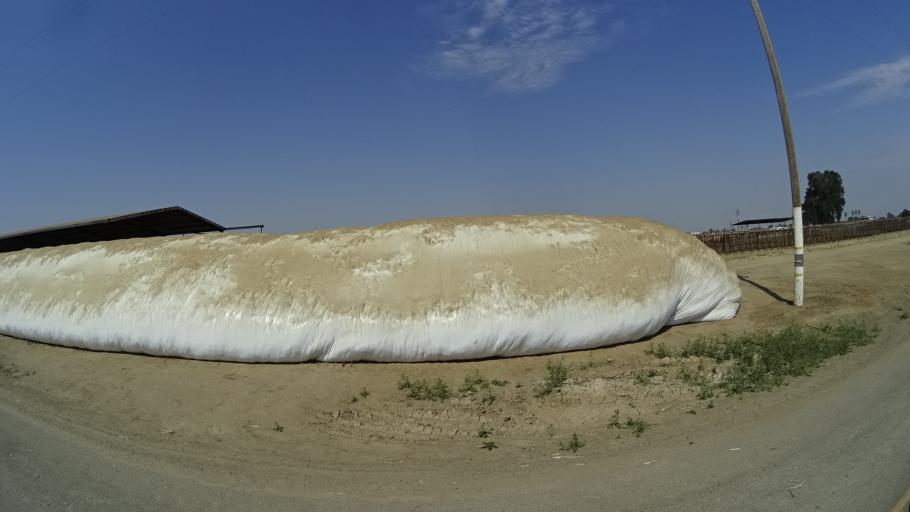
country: US
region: California
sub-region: Fresno County
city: Riverdale
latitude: 36.3969
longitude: -119.7804
